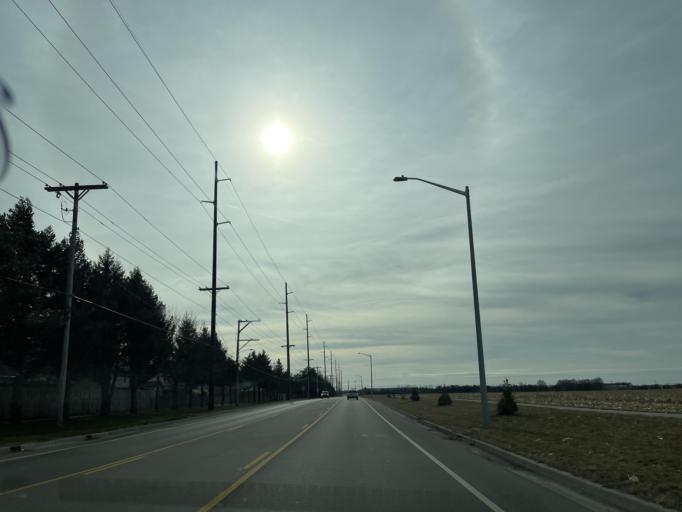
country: US
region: Illinois
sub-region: Sangamon County
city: Jerome
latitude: 39.7659
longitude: -89.7346
